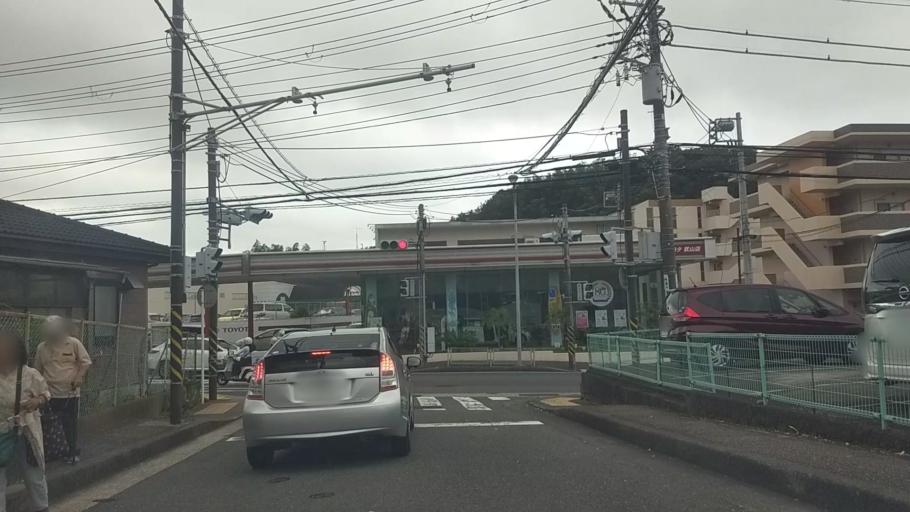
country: JP
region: Kanagawa
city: Yokosuka
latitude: 35.2303
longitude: 139.6530
